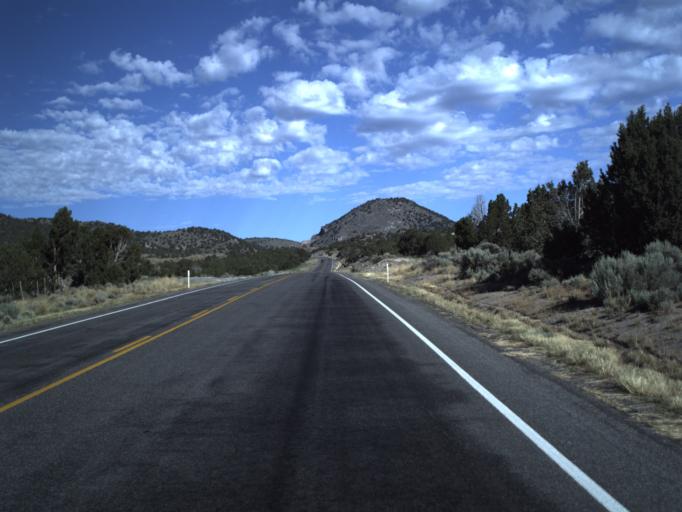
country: US
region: Utah
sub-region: Utah County
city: Genola
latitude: 39.9652
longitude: -112.0474
